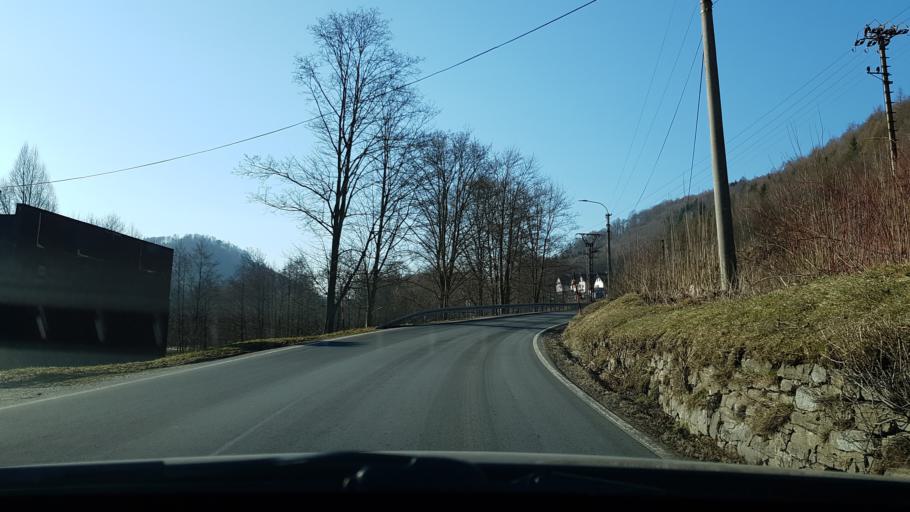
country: CZ
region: Olomoucky
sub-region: Okres Sumperk
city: Hanusovice
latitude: 50.0659
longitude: 16.9255
